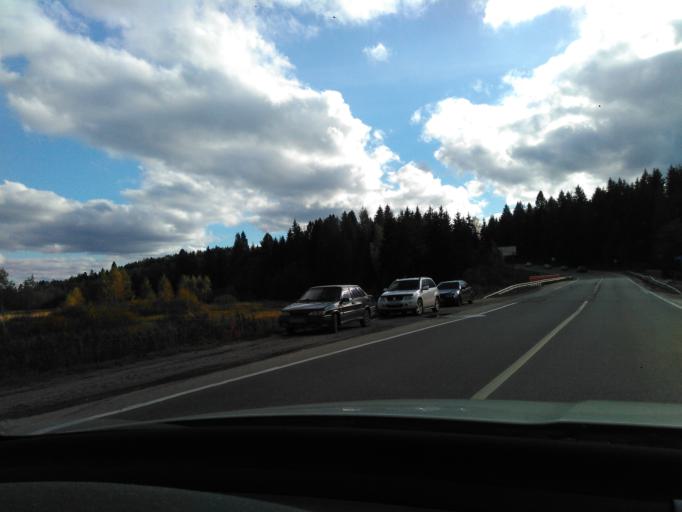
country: RU
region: Moskovskaya
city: Solnechnogorsk
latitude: 56.1203
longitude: 36.9293
